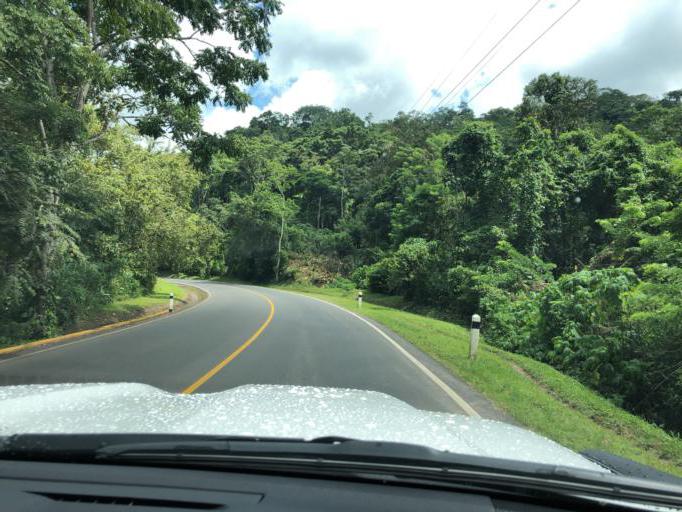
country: NI
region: Chontales
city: Villa Sandino
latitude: 11.9939
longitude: -84.9037
